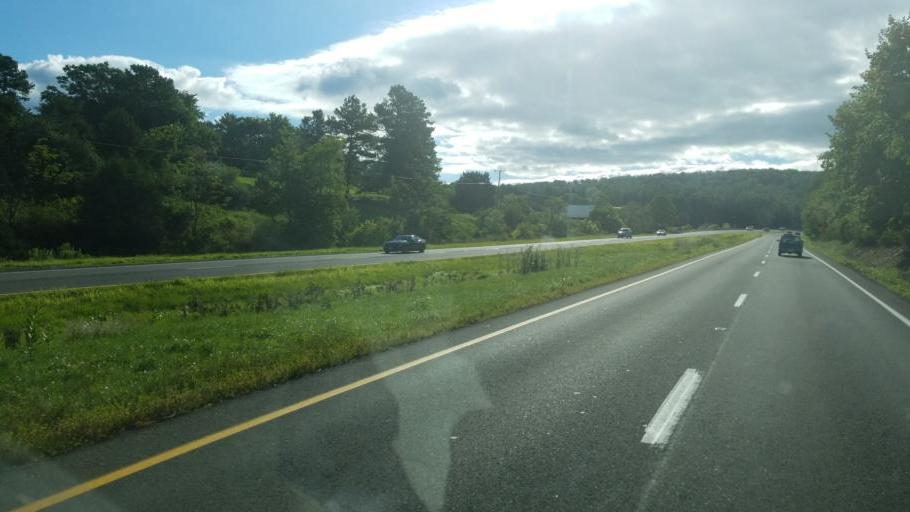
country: US
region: Virginia
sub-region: City of Winchester
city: Winchester
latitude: 39.2489
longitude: -78.2093
